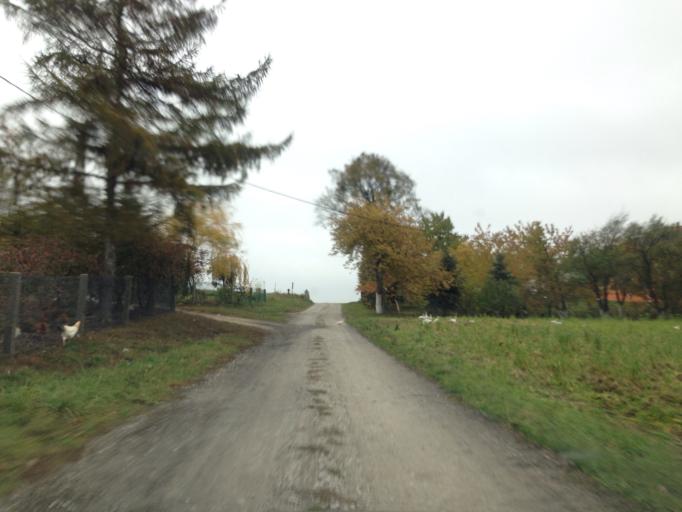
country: PL
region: Kujawsko-Pomorskie
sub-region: Powiat brodnicki
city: Gorzno
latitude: 53.2044
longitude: 19.6187
